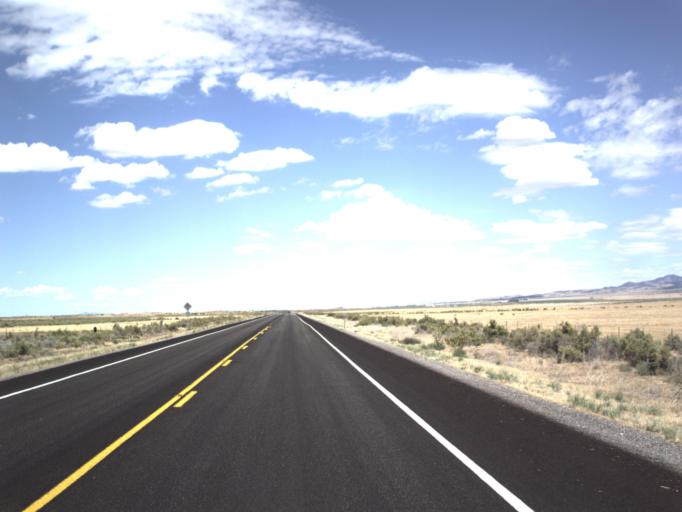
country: US
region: Utah
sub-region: Millard County
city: Fillmore
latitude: 39.1206
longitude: -112.3565
